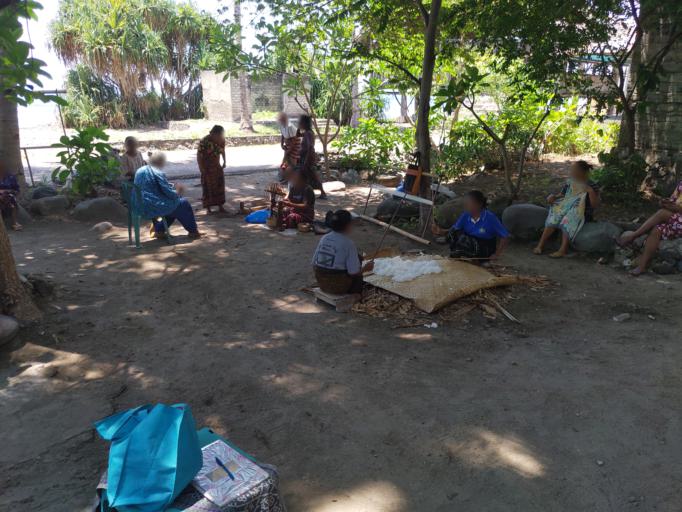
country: ID
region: East Nusa Tenggara
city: Sikka
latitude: -8.7499
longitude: 122.1968
